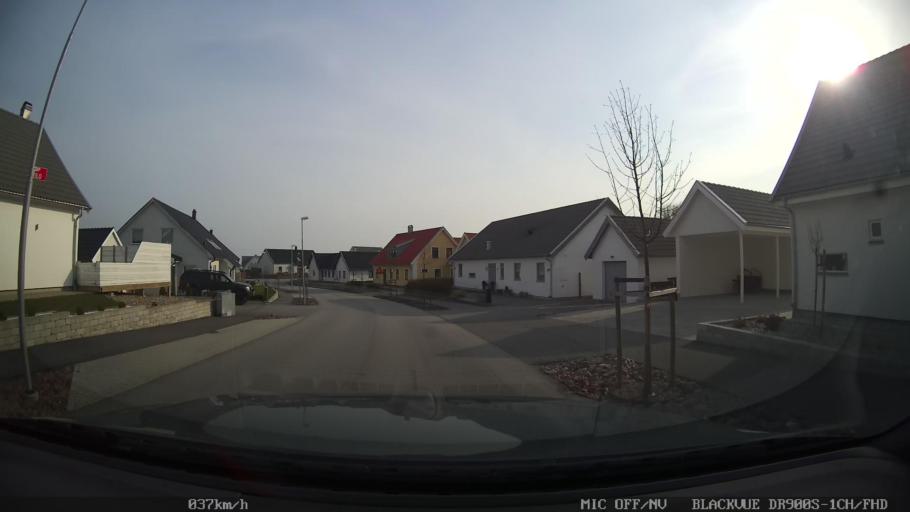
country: SE
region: Skane
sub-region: Ystads Kommun
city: Ystad
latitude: 55.4454
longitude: 13.7947
